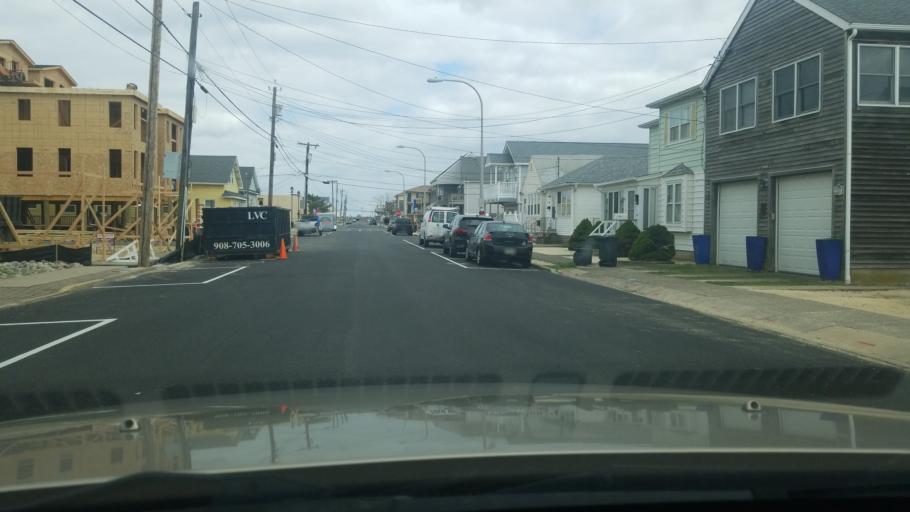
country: US
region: New Jersey
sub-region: Ocean County
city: Seaside Heights
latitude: 39.9449
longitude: -74.0746
